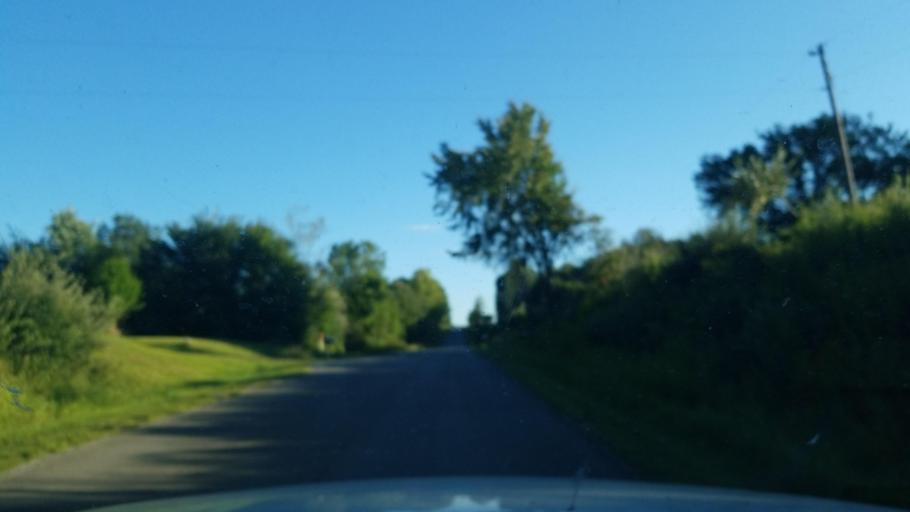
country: US
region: Illinois
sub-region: Hardin County
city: Elizabethtown
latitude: 37.5878
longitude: -88.3655
